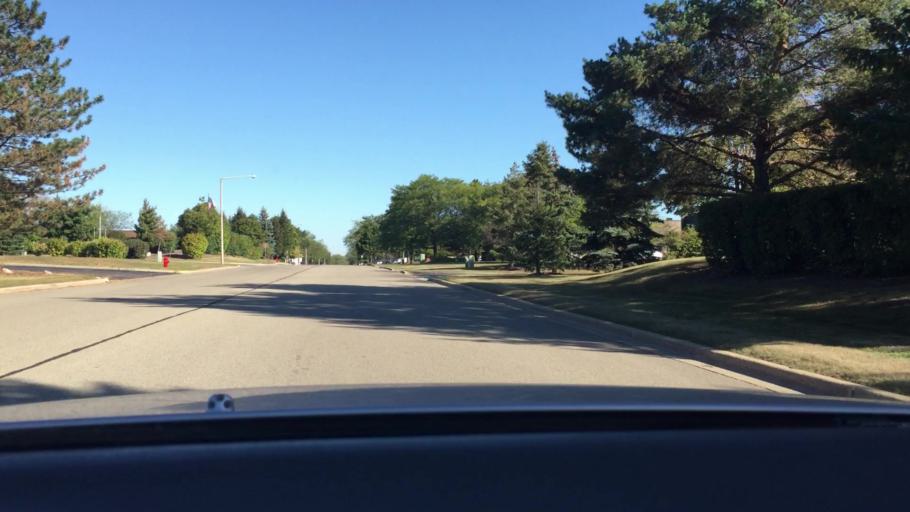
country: US
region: Illinois
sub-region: Lake County
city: Forest Lake
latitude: 42.2050
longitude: -88.0676
